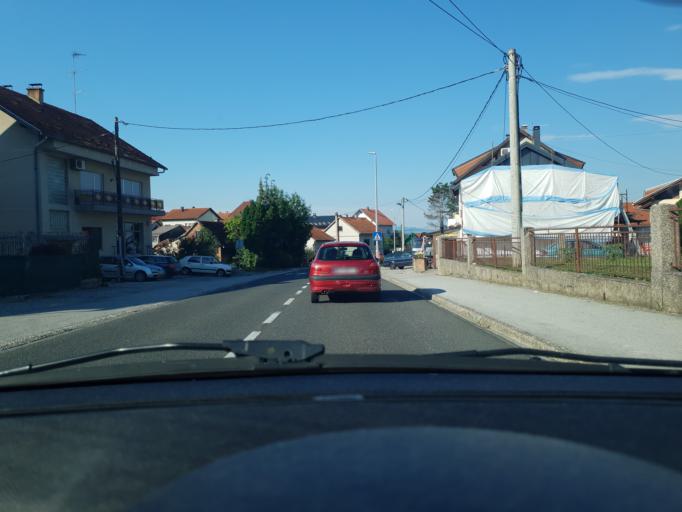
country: HR
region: Krapinsko-Zagorska
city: Oroslavje
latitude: 45.9971
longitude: 15.9147
